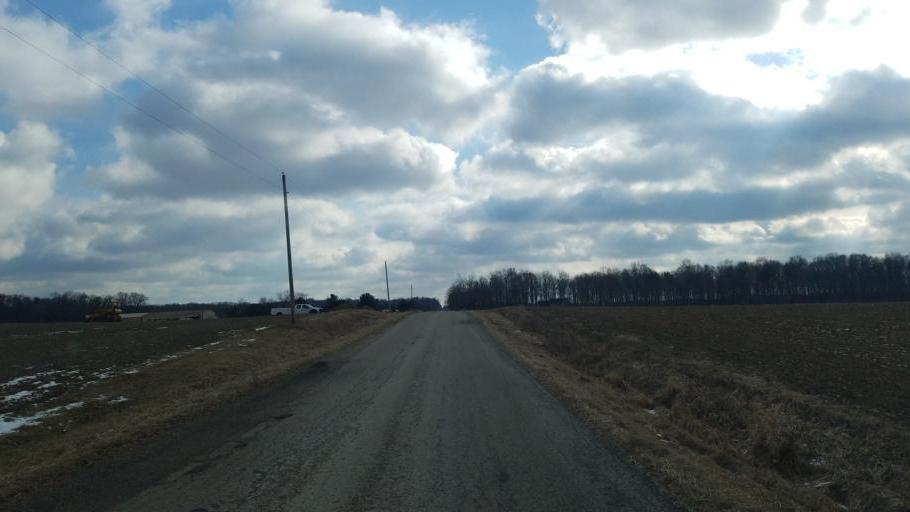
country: US
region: Ohio
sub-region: Crawford County
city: Galion
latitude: 40.6729
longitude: -82.7466
